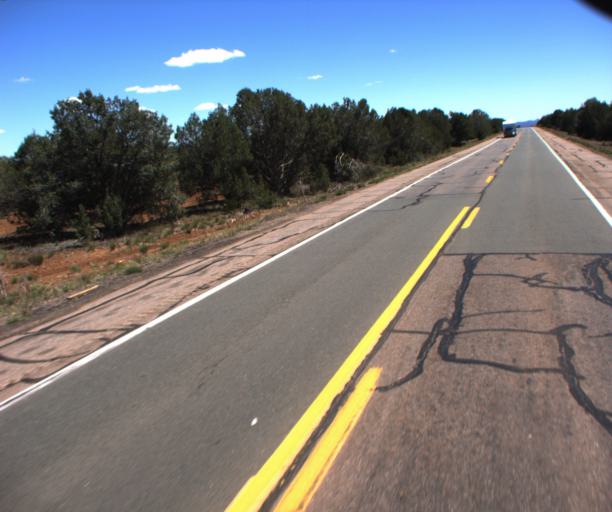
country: US
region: Arizona
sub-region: Yavapai County
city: Paulden
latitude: 35.0756
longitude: -112.4028
